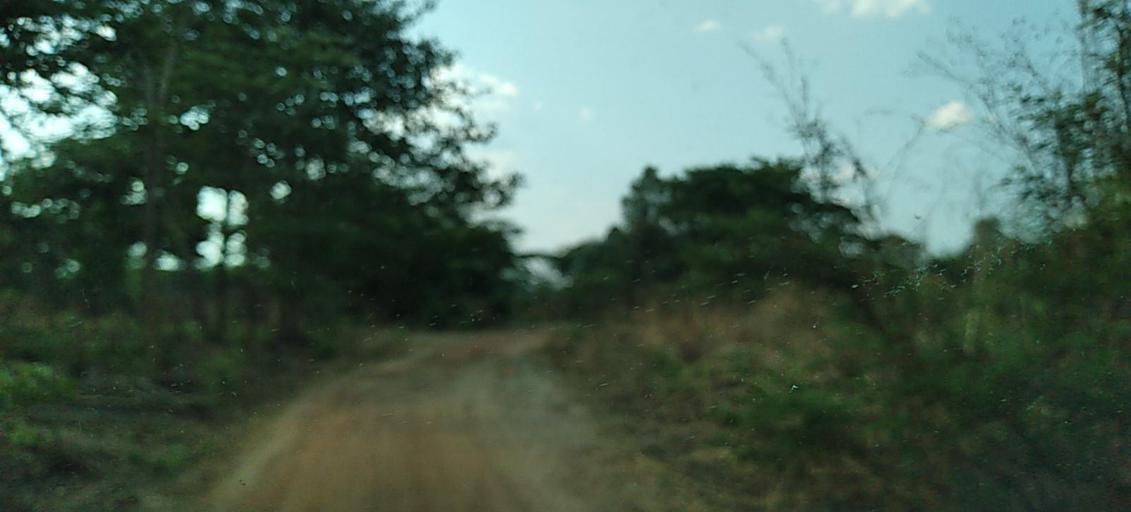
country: ZM
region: Copperbelt
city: Mpongwe
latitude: -13.4691
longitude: 28.0698
